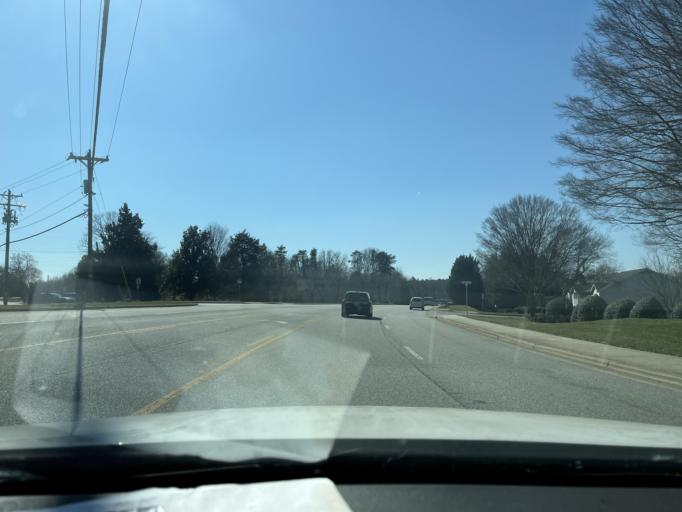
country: US
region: North Carolina
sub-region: Guilford County
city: Jamestown
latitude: 36.0561
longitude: -79.9129
